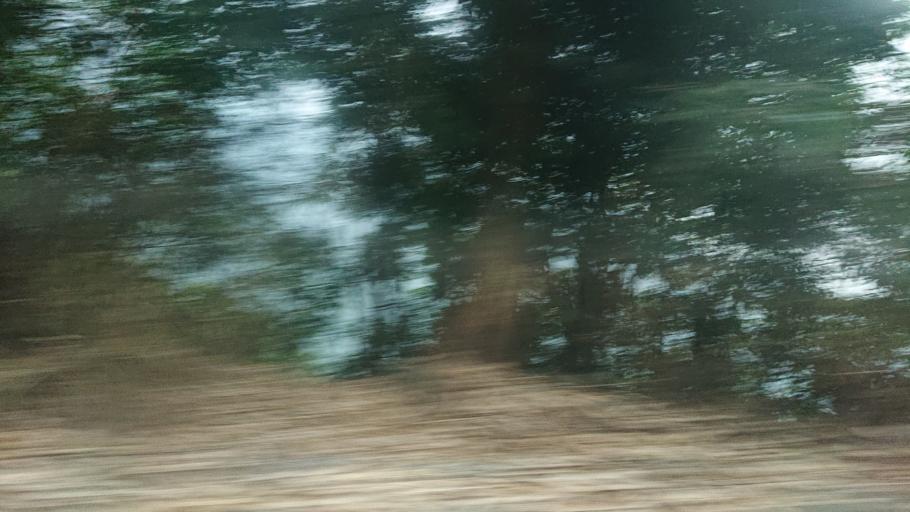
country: TW
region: Taiwan
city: Lugu
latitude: 23.5935
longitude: 120.7169
